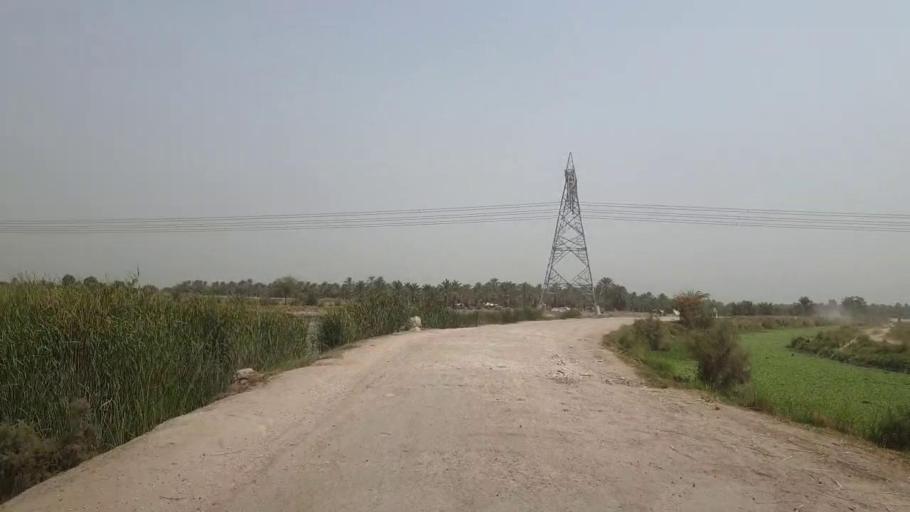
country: PK
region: Sindh
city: Gambat
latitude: 27.4124
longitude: 68.5499
